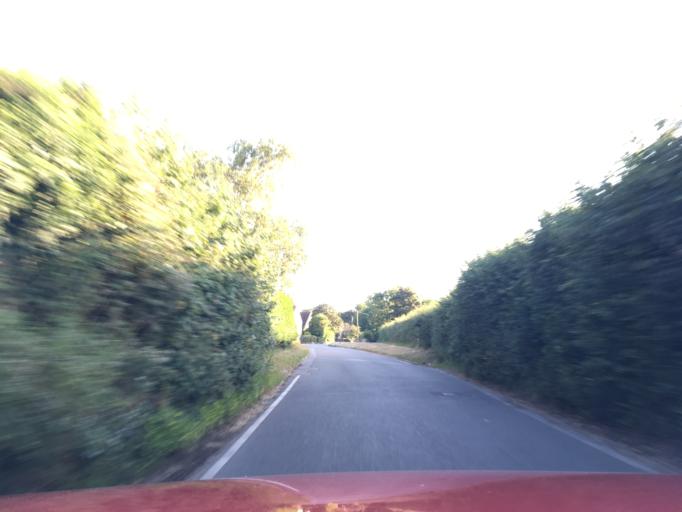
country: GB
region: England
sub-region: Hampshire
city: Tadley
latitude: 51.4162
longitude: -1.1518
